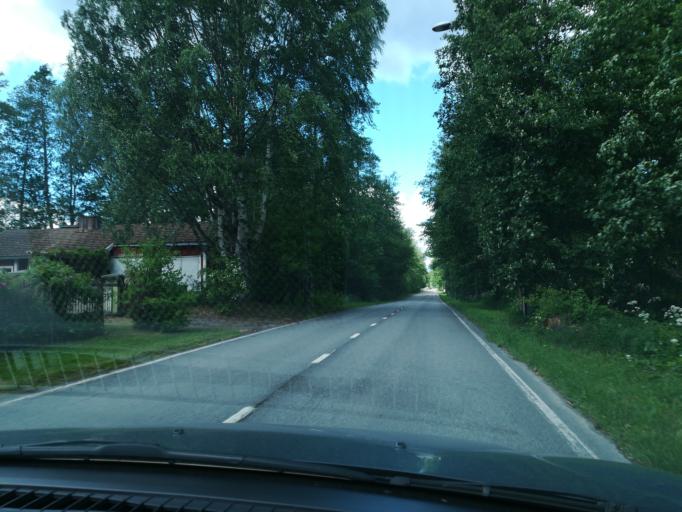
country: FI
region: Southern Savonia
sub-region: Mikkeli
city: Hirvensalmi
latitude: 61.6377
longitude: 26.7800
